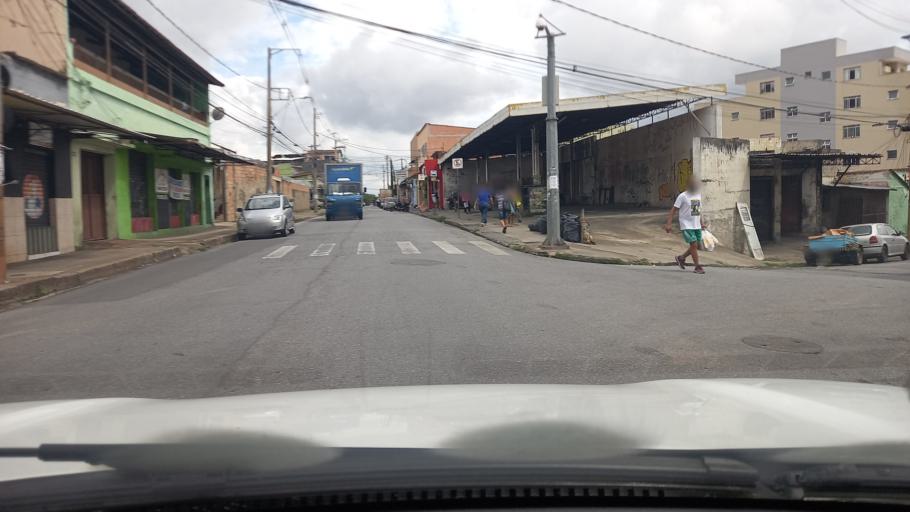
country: BR
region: Minas Gerais
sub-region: Contagem
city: Contagem
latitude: -19.9096
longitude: -44.0036
